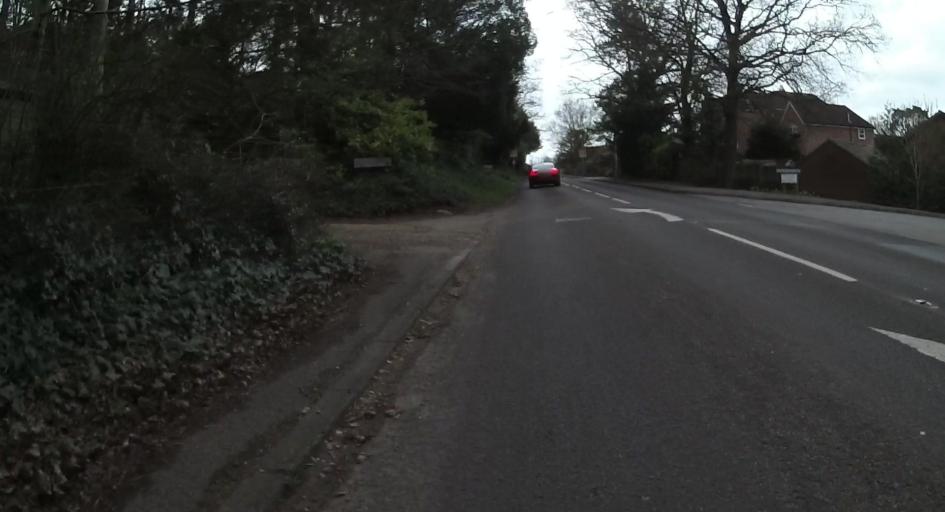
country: GB
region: England
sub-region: Surrey
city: Farnham
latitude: 51.1928
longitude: -0.7891
